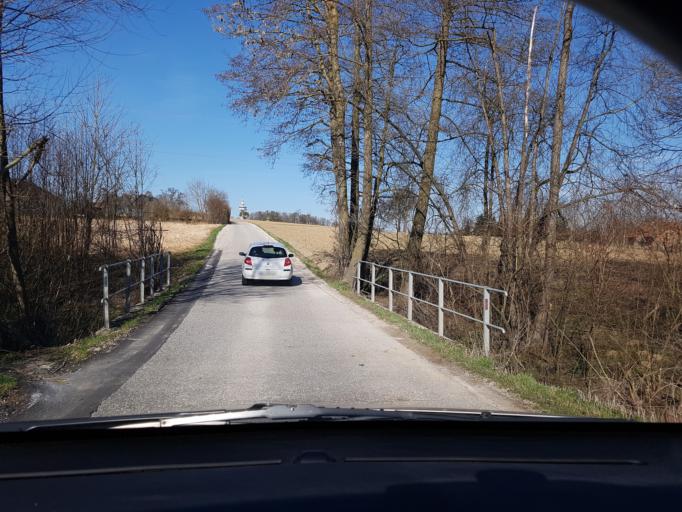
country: AT
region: Upper Austria
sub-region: Politischer Bezirk Linz-Land
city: Ansfelden
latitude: 48.1972
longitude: 14.3129
